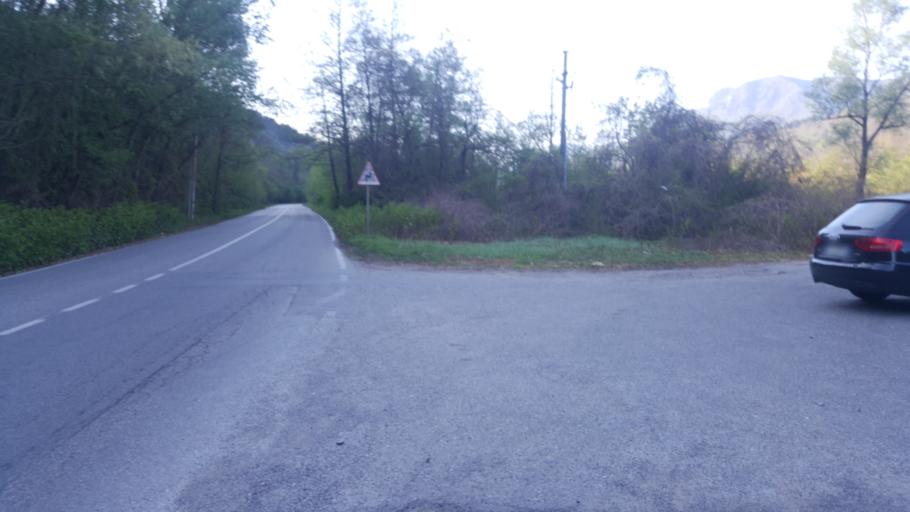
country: IT
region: Lombardy
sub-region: Provincia di Varese
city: Montegrino Valtravaglia
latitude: 45.9804
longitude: 8.7497
